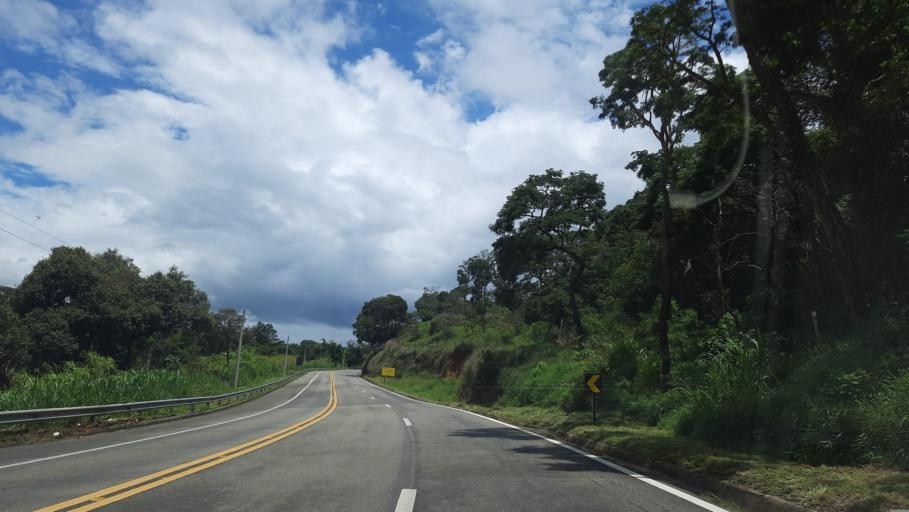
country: BR
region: Sao Paulo
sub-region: Vargem Grande Do Sul
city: Vargem Grande do Sul
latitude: -21.8328
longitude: -46.7536
